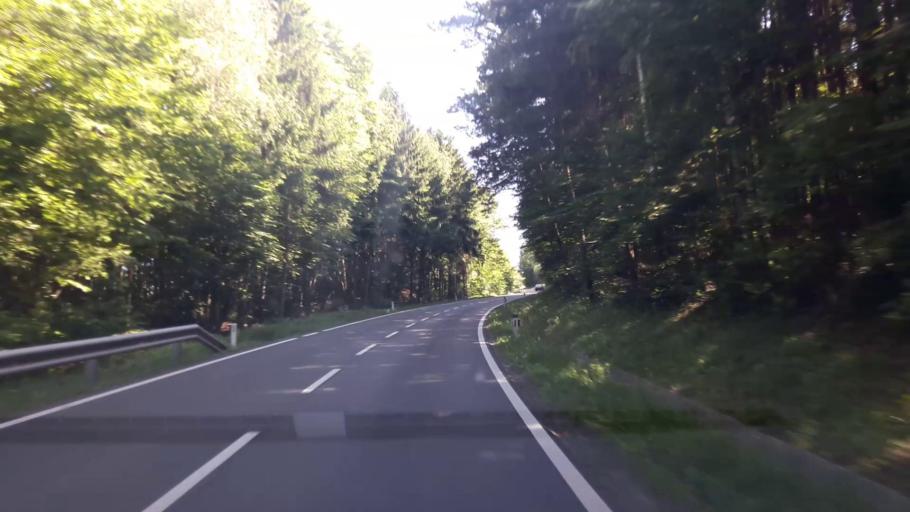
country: AT
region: Styria
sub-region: Politischer Bezirk Hartberg-Fuerstenfeld
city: Neudau
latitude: 47.1570
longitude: 16.1198
